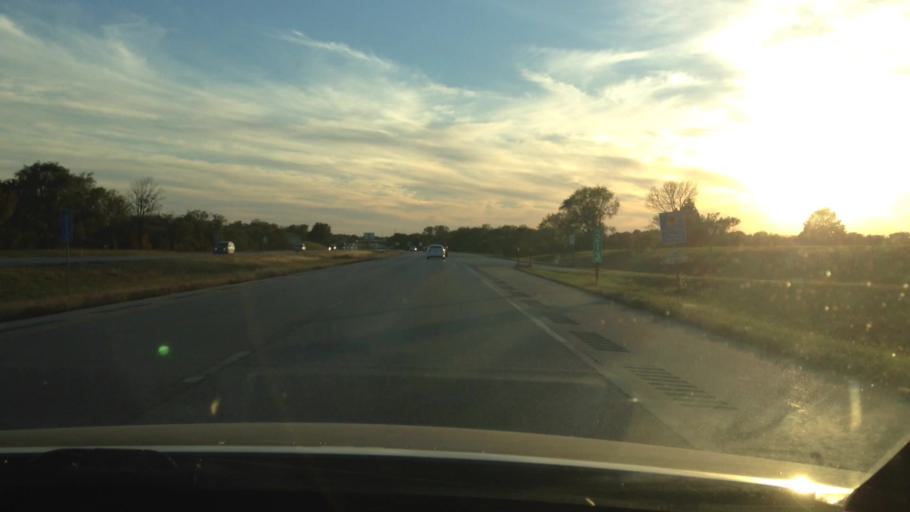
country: US
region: Kansas
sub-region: Johnson County
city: Olathe
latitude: 38.8310
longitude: -94.8512
